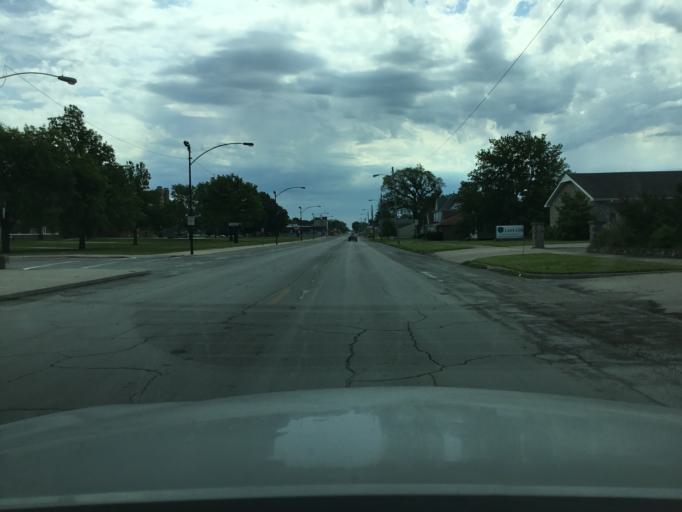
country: US
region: Kansas
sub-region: Montgomery County
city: Coffeyville
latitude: 37.0362
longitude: -95.6342
